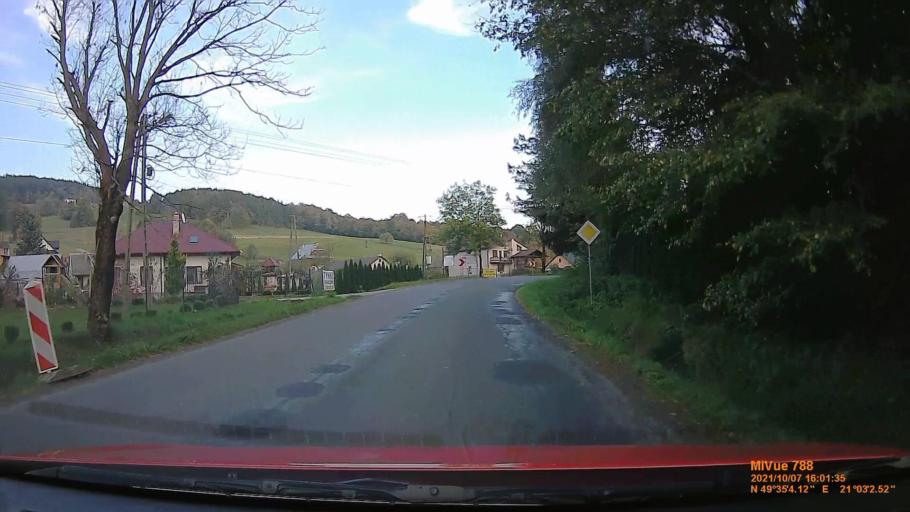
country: PL
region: Lesser Poland Voivodeship
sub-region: Powiat gorlicki
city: Ropa
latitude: 49.5845
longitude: 21.0507
